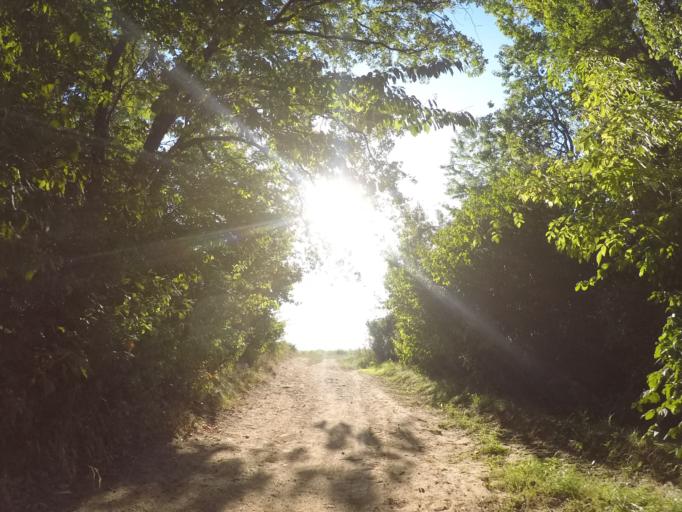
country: SK
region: Kosicky
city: Kosice
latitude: 48.7296
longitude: 21.1986
